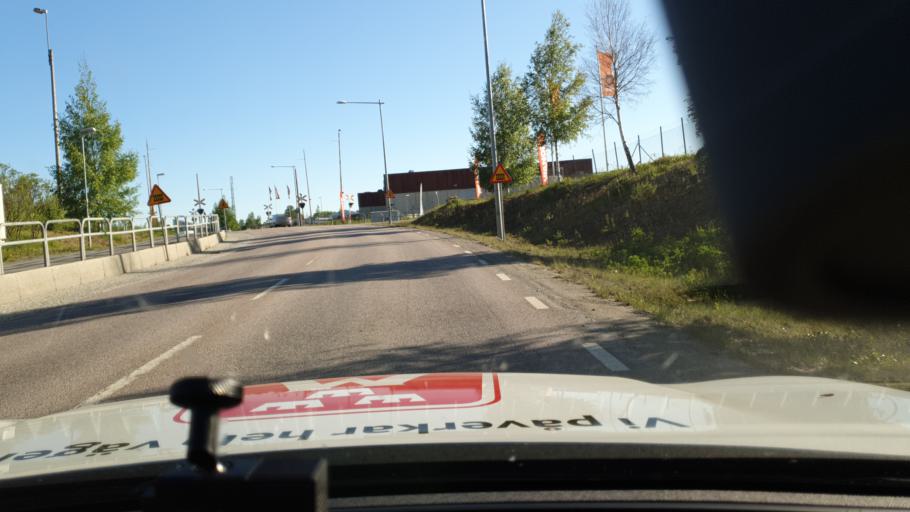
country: SE
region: Vaesterbotten
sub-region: Umea Kommun
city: Umea
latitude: 63.8379
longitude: 20.2478
